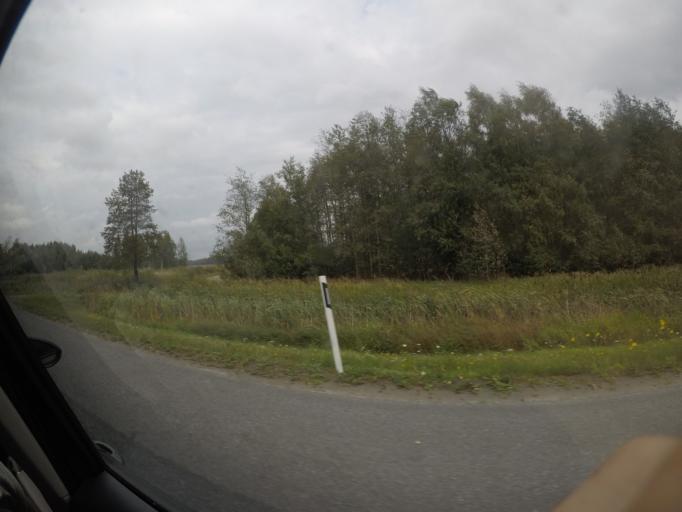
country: FI
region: Haeme
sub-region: Haemeenlinna
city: Parola
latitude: 61.0380
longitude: 24.4058
